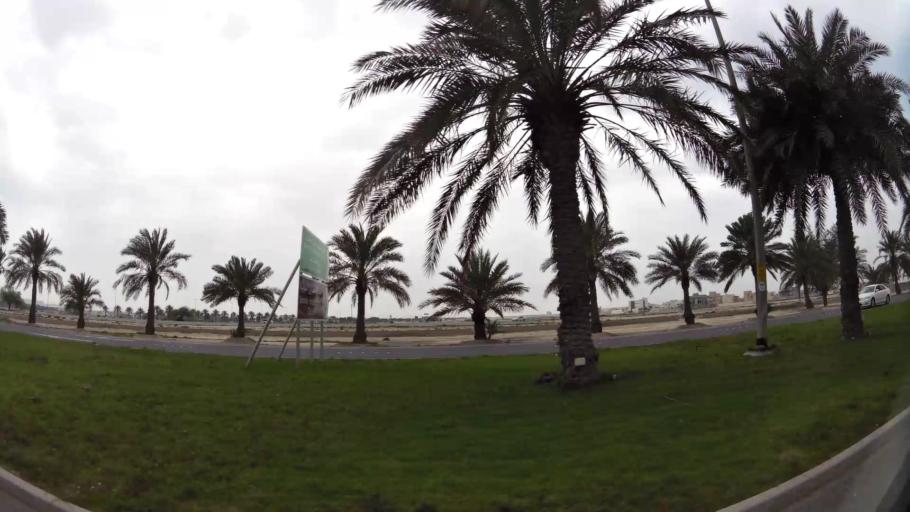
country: BH
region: Central Governorate
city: Dar Kulayb
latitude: 26.0564
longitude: 50.4973
